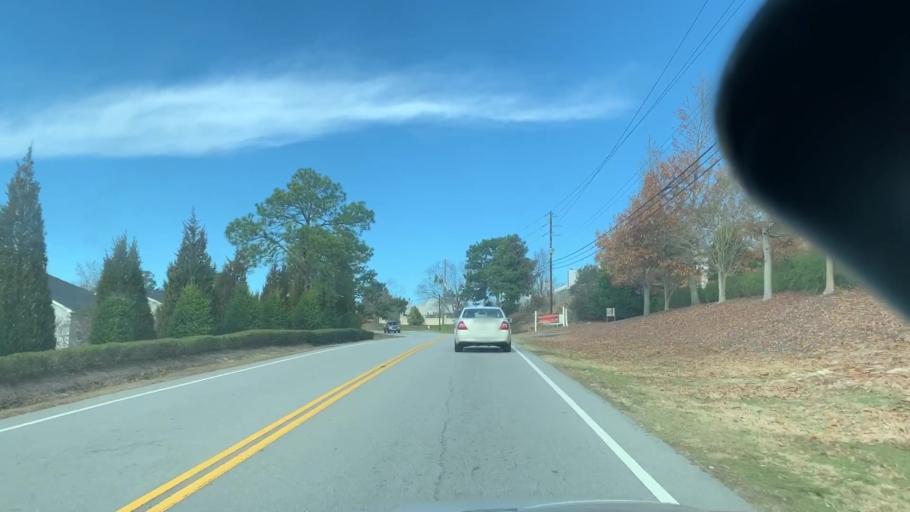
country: US
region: South Carolina
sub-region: Richland County
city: Woodfield
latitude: 34.1047
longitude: -80.8973
